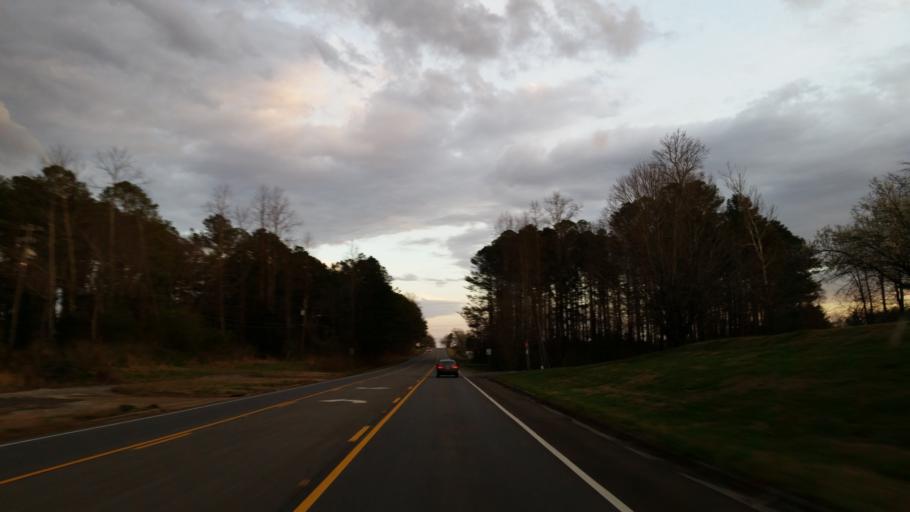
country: US
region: Georgia
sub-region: Pickens County
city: Jasper
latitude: 34.4591
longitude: -84.4125
